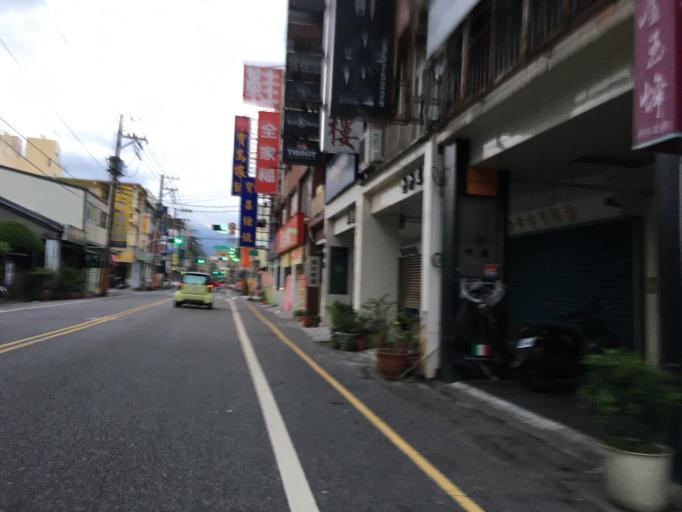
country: TW
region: Taiwan
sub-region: Yilan
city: Yilan
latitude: 24.6756
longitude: 121.7713
